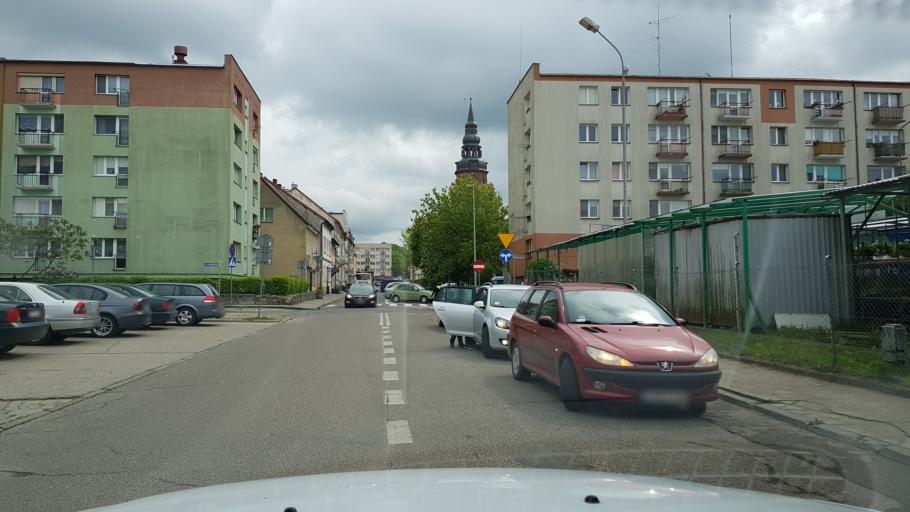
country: PL
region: West Pomeranian Voivodeship
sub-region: Powiat gryfinski
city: Gryfino
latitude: 53.2536
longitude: 14.4845
